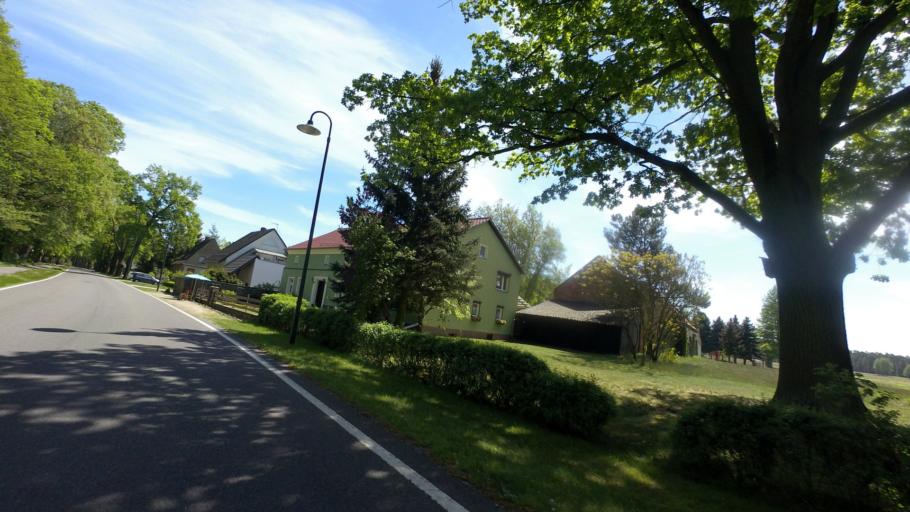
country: DE
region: Brandenburg
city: Luckenwalde
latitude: 52.0487
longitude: 13.2763
